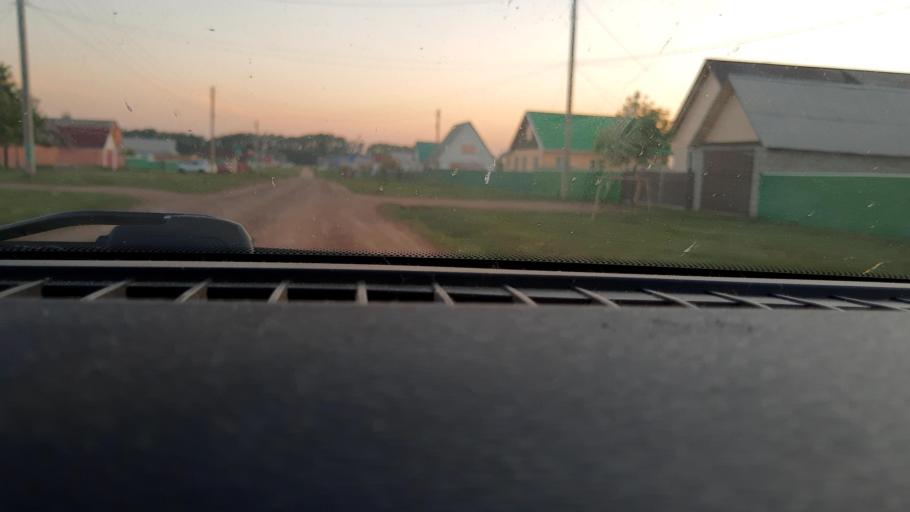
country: RU
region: Bashkortostan
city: Alekseyevka
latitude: 54.7169
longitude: 55.0066
